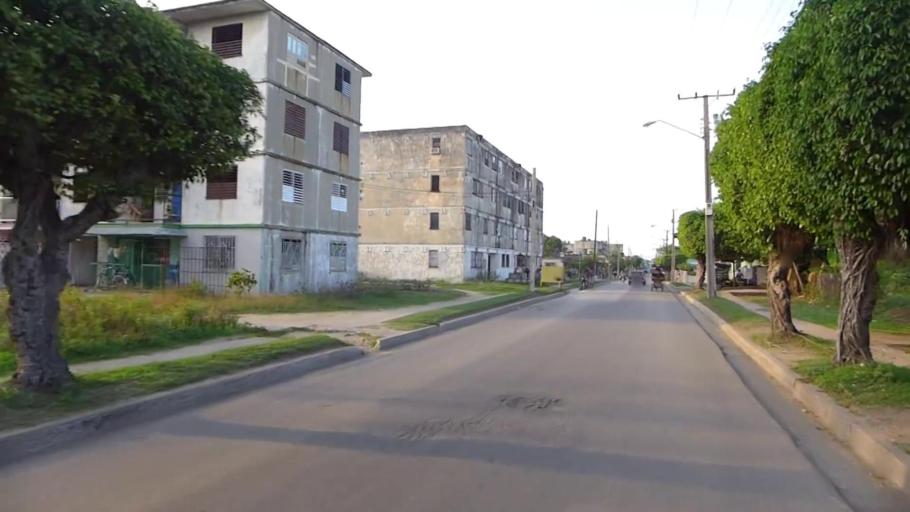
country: CU
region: Camaguey
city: Camaguey
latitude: 21.3787
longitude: -77.9374
